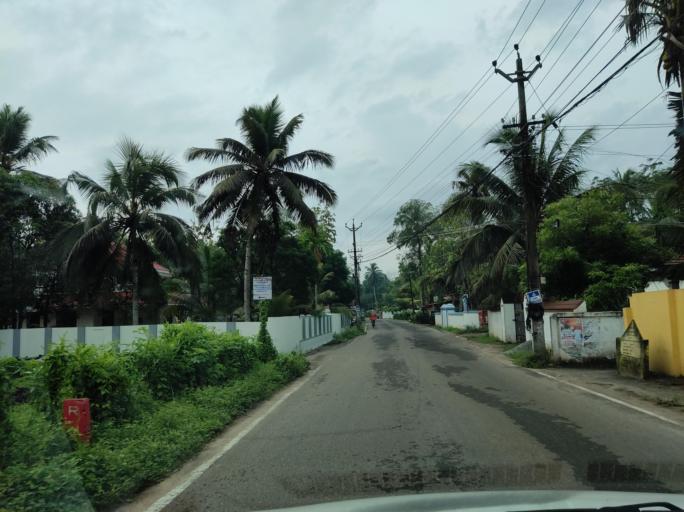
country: IN
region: Kerala
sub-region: Alappuzha
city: Kayankulam
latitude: 9.2077
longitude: 76.4620
